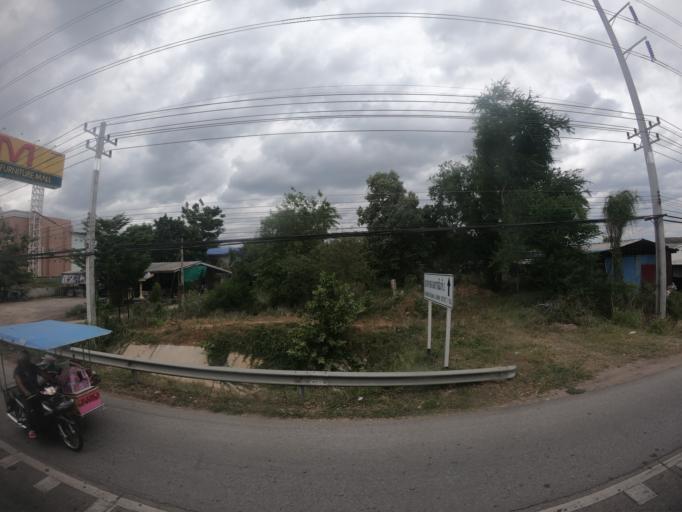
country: TH
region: Nakhon Ratchasima
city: Nakhon Ratchasima
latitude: 14.9256
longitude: 102.1420
